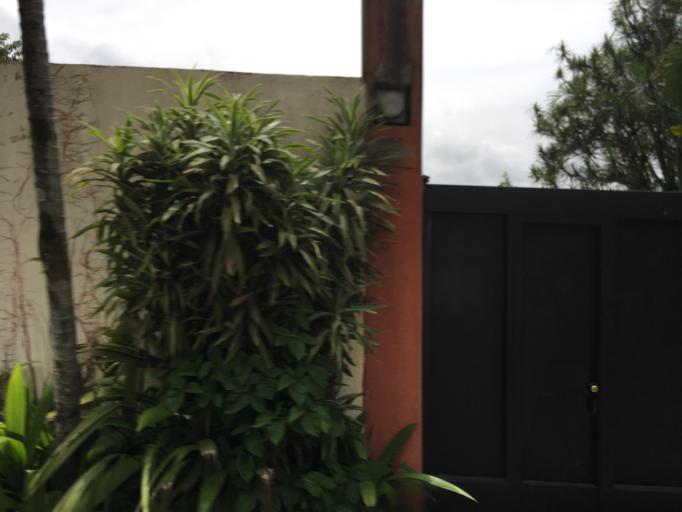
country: GT
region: Guatemala
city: Villa Canales
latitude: 14.4437
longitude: -90.5629
